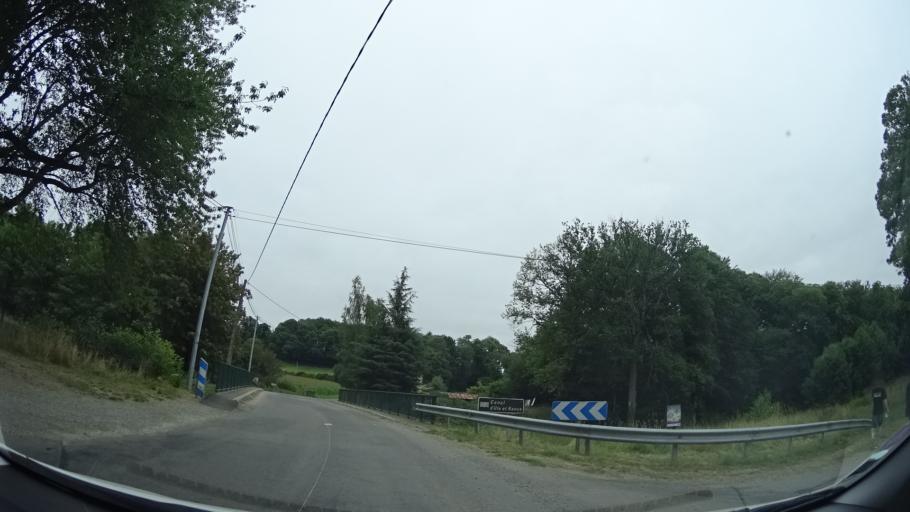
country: FR
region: Brittany
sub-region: Departement d'Ille-et-Vilaine
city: Hede-Bazouges
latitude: 48.3018
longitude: -1.7720
